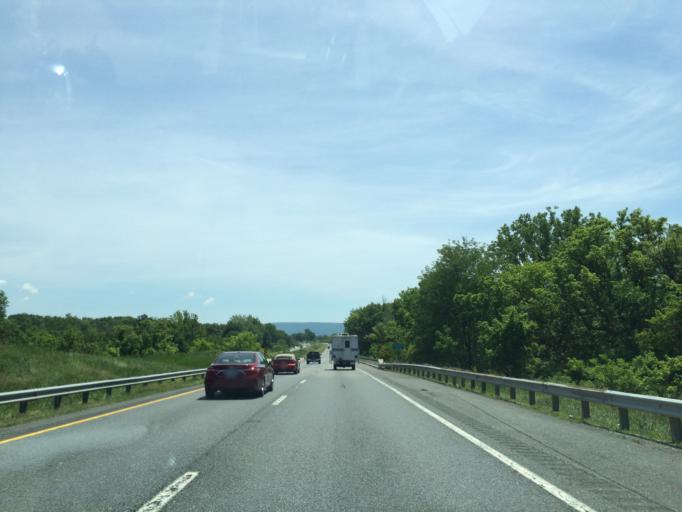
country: US
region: Maryland
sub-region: Washington County
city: Hagerstown
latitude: 39.6031
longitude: -77.7135
